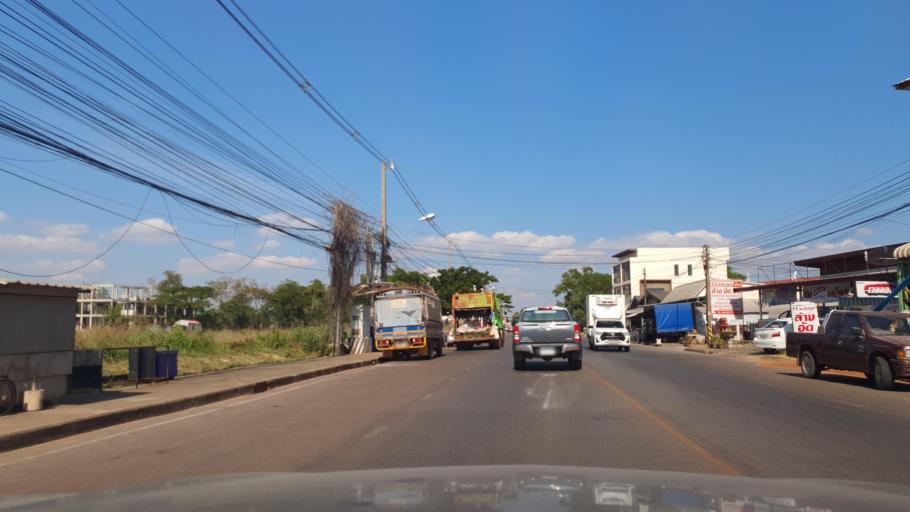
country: TH
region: Sakon Nakhon
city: Sakon Nakhon
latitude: 17.1723
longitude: 104.1265
